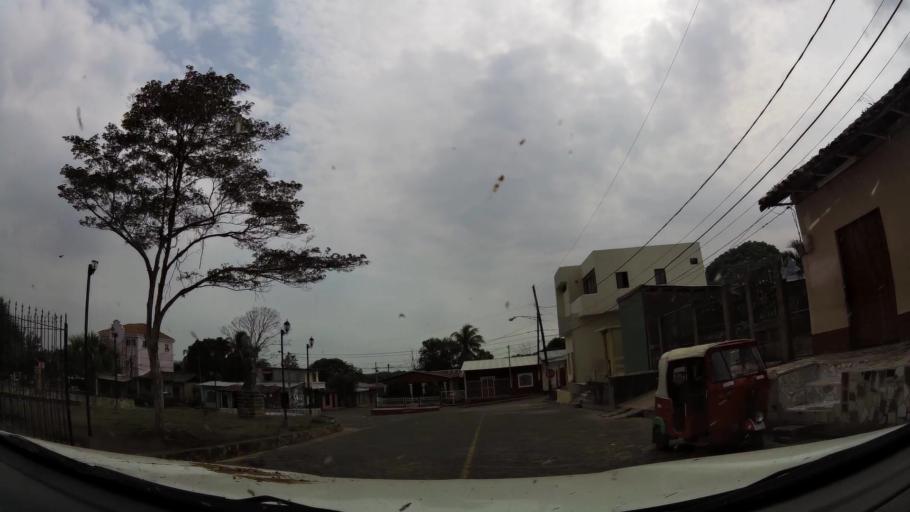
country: NI
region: Granada
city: Diria
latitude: 11.8868
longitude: -86.0563
